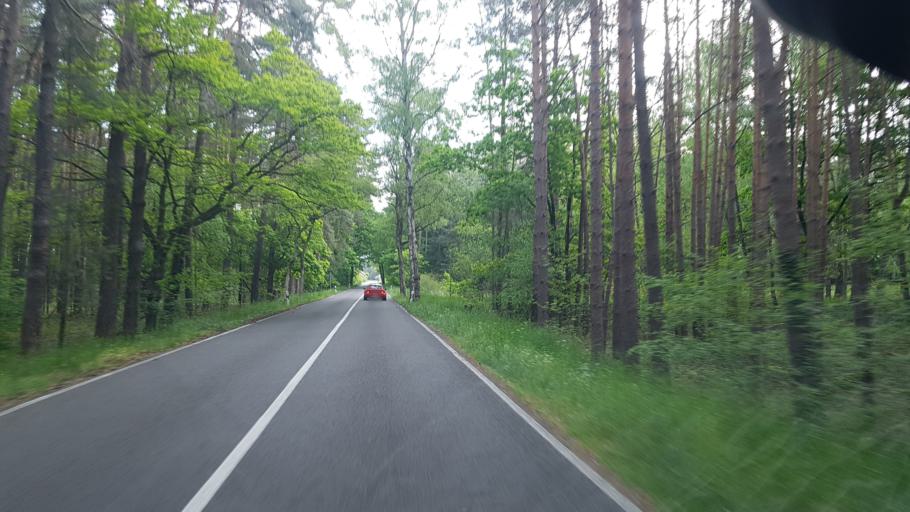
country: DE
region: Brandenburg
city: Baruth
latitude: 51.9839
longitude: 13.4786
